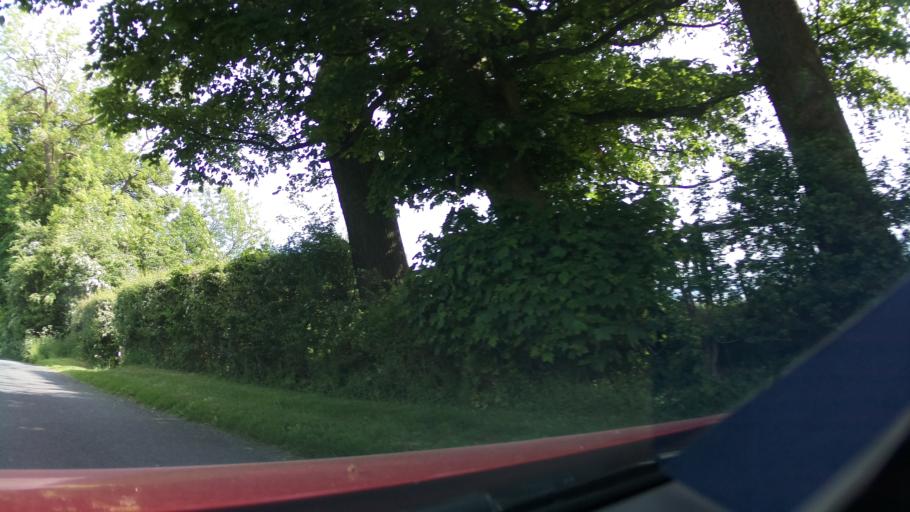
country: GB
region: England
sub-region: Gloucestershire
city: Chipping Campden
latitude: 52.0555
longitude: -1.8041
